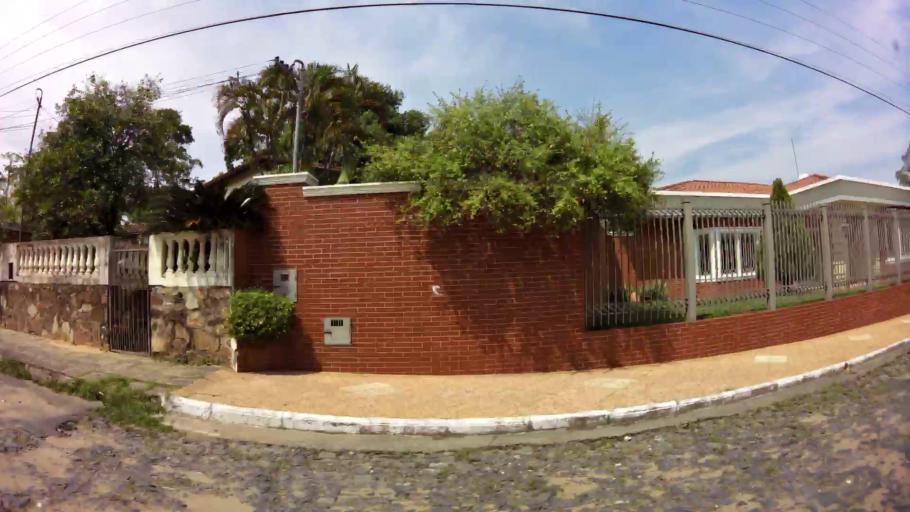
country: PY
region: Asuncion
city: Asuncion
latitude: -25.2649
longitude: -57.5849
